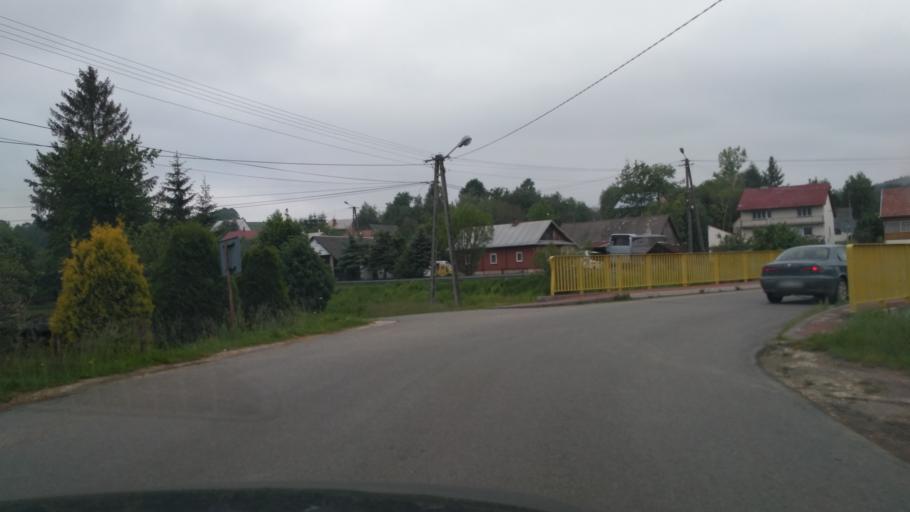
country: PL
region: Subcarpathian Voivodeship
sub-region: Powiat ropczycko-sedziszowski
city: Zagorzyce
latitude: 50.0151
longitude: 21.6753
